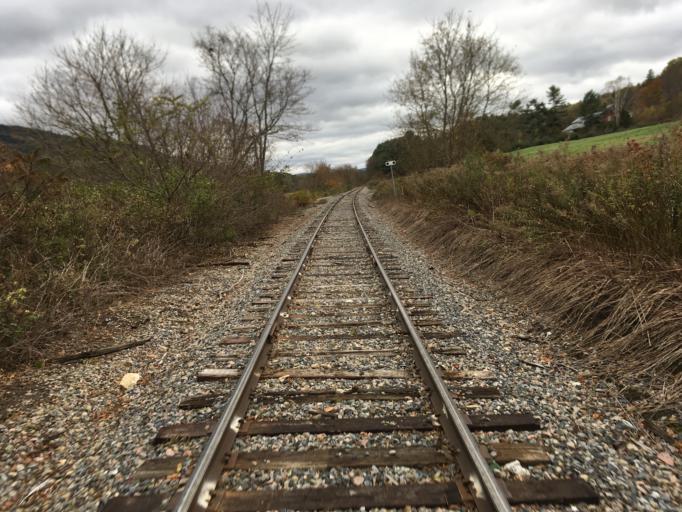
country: US
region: New Hampshire
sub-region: Grafton County
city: Woodsville
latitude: 44.1839
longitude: -72.0612
